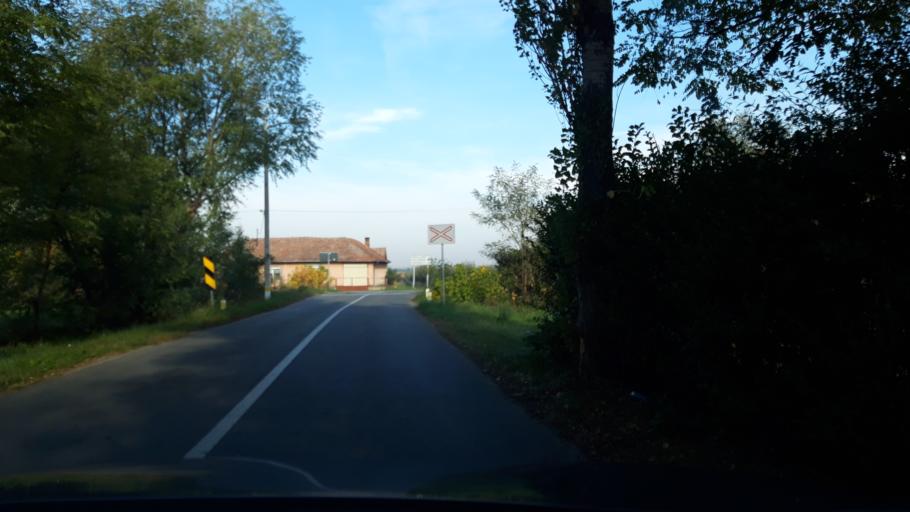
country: HU
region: Csongrad
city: Asotthalom
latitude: 46.1253
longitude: 19.8500
